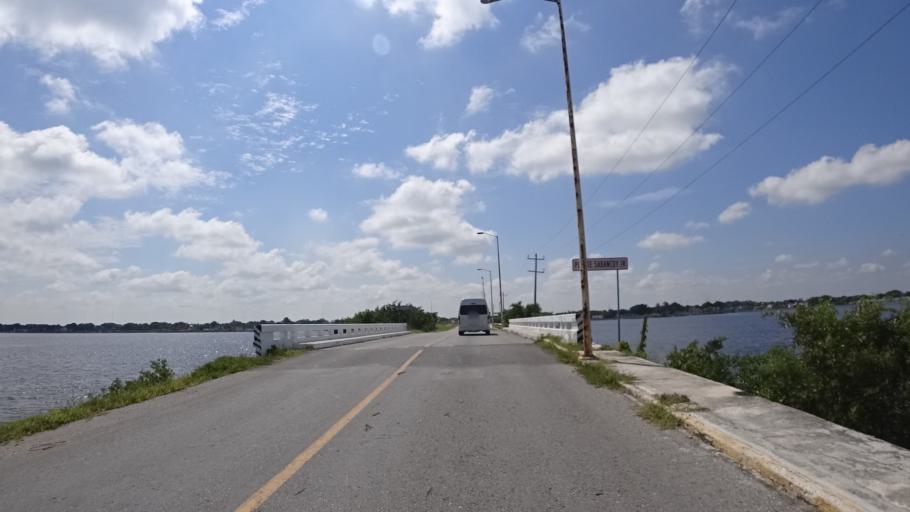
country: MX
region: Campeche
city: Sabancuy
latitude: 18.9800
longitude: -91.1832
